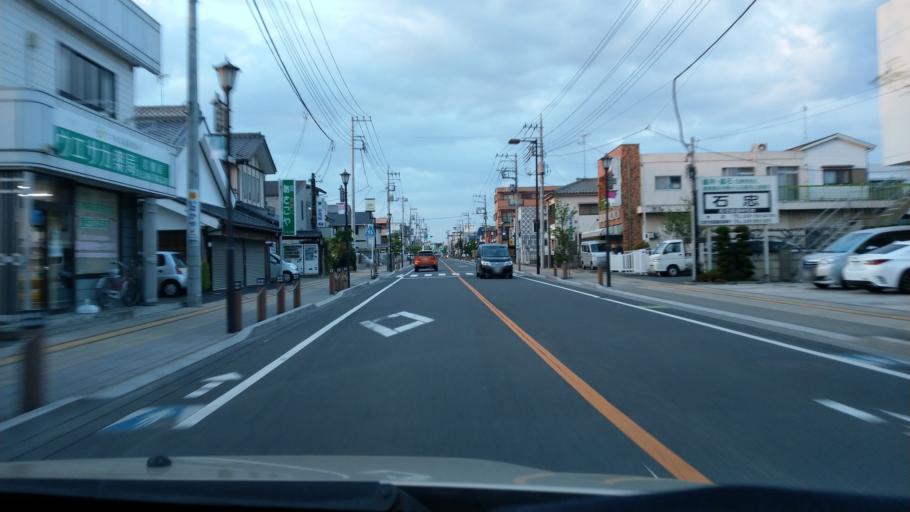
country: JP
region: Saitama
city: Iwatsuki
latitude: 35.9456
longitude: 139.6933
